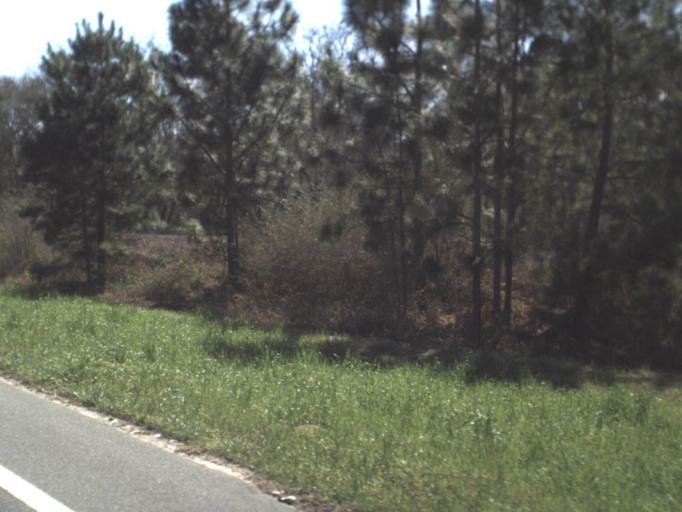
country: US
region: Florida
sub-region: Gadsden County
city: Gretna
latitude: 30.6438
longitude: -84.6780
